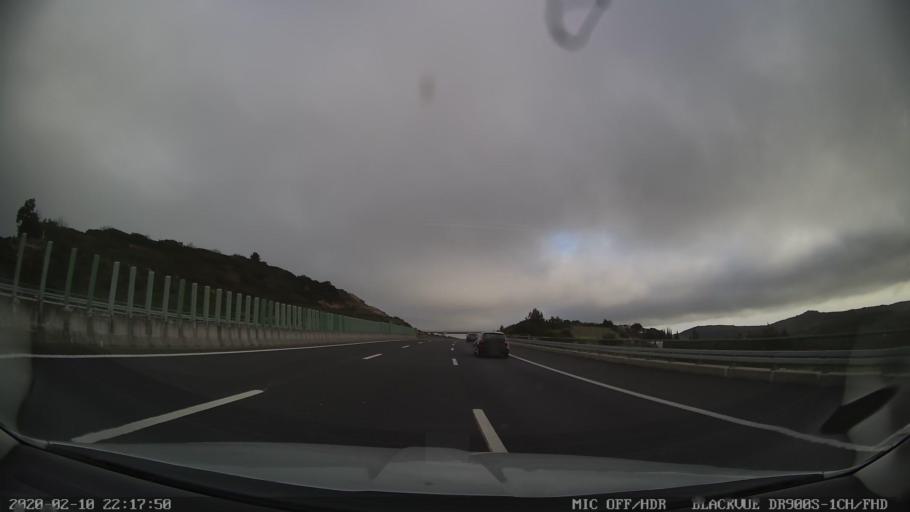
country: PT
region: Lisbon
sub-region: Loures
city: Bucelas
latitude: 38.9249
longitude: -9.0758
